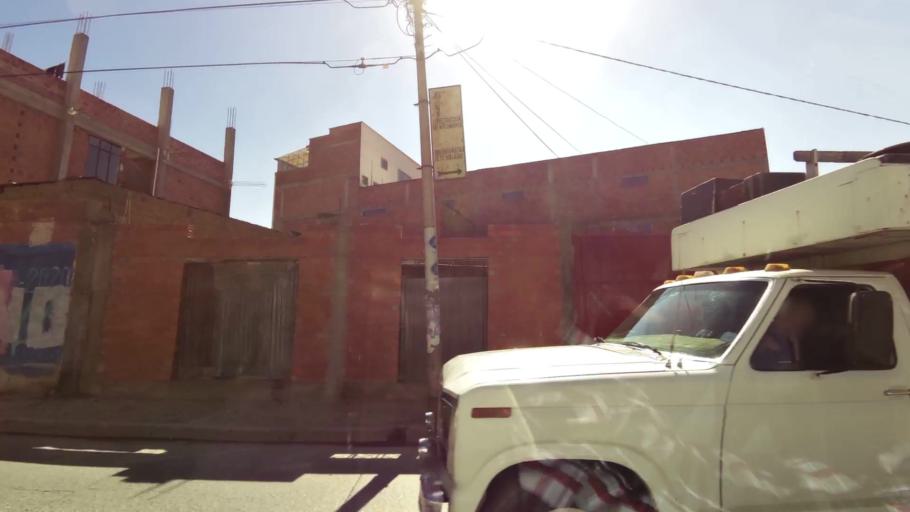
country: BO
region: La Paz
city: La Paz
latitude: -16.5185
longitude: -68.1614
